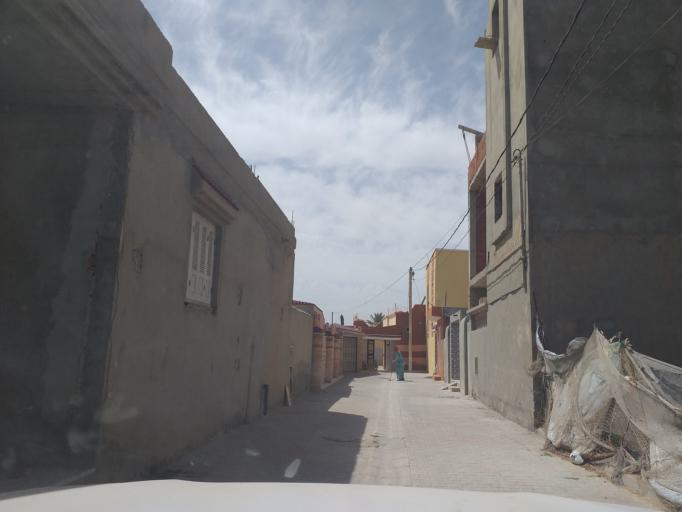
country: TN
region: Qabis
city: Gabes
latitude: 33.9495
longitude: 10.0658
